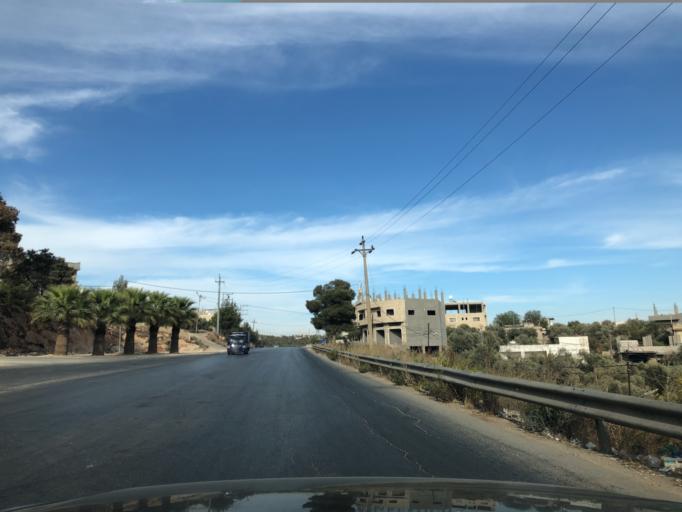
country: JO
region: Irbid
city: Raymun
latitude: 32.2861
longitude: 35.8280
